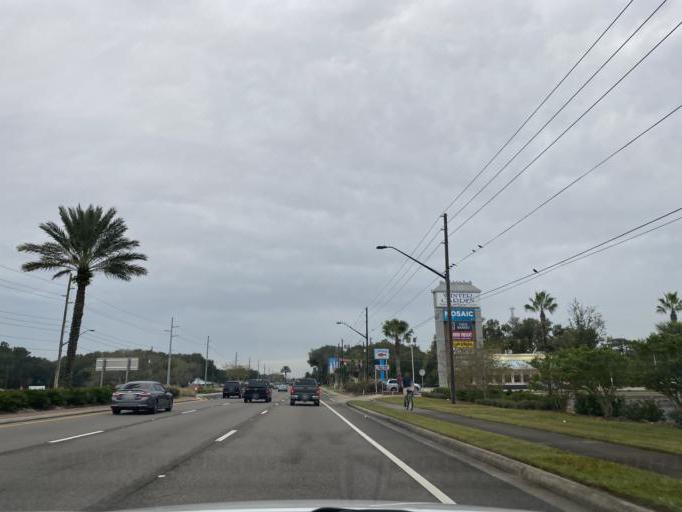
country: US
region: Florida
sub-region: Orange County
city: Winter Garden
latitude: 28.5512
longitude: -81.5943
